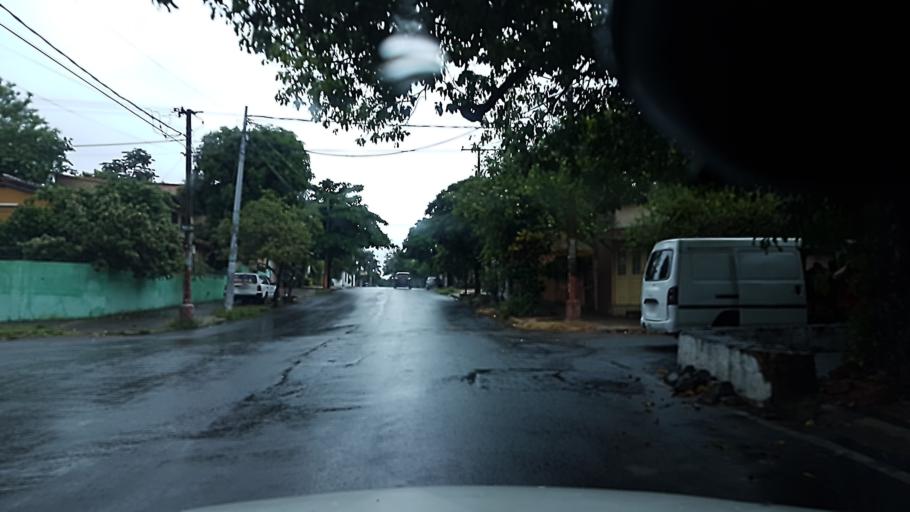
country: PY
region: Central
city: Lambare
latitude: -25.3276
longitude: -57.5817
